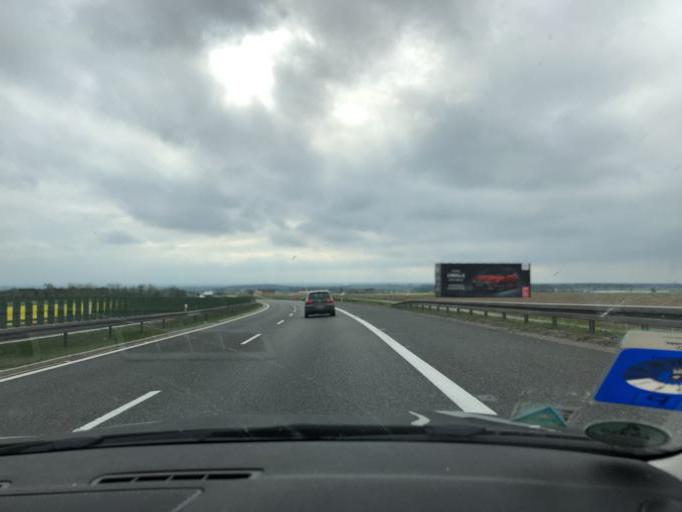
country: PL
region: Opole Voivodeship
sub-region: Powiat krapkowicki
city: Rozwadza
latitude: 50.4819
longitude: 18.1150
